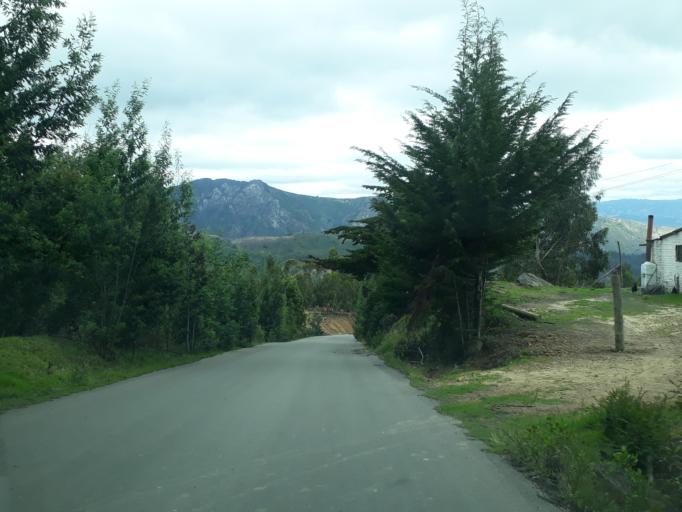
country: CO
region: Cundinamarca
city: Cucunuba
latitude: 5.2195
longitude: -73.7824
